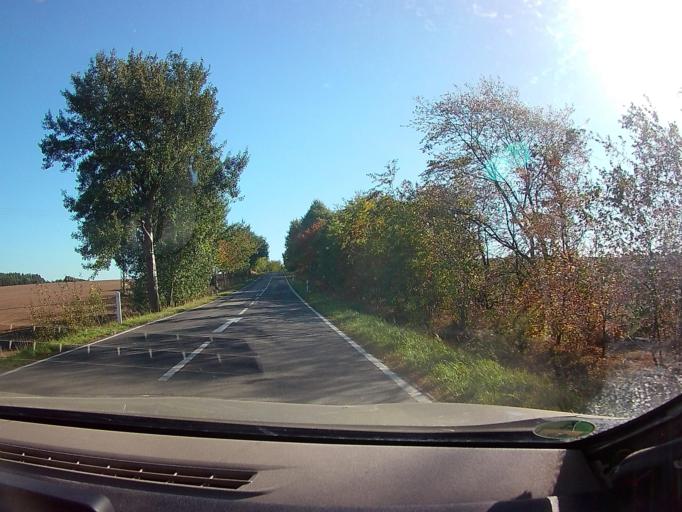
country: DE
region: Mecklenburg-Vorpommern
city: Rechlin
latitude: 53.2426
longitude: 12.7767
